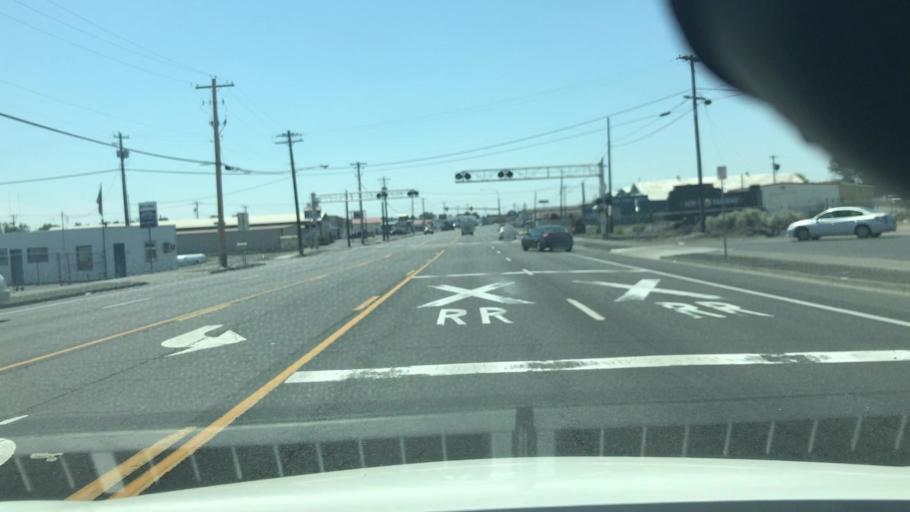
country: US
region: Washington
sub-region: Grant County
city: Moses Lake
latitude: 47.1186
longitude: -119.2946
